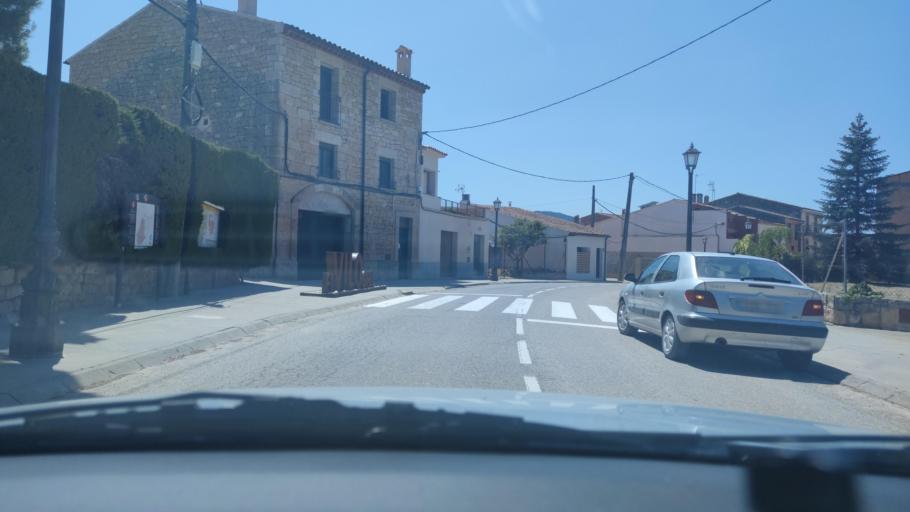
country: ES
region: Catalonia
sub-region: Provincia de Tarragona
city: Vallclara
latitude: 41.3840
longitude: 0.9484
